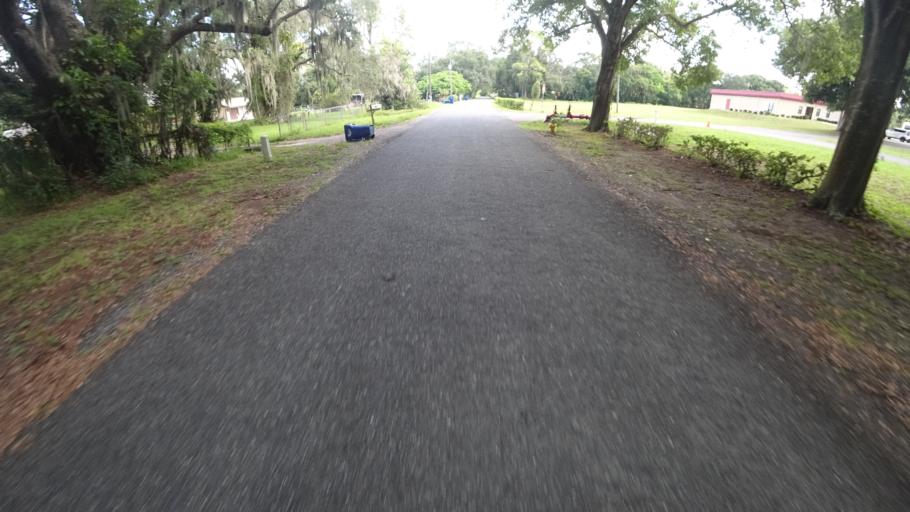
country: US
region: Florida
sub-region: Manatee County
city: Samoset
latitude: 27.4483
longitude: -82.5415
